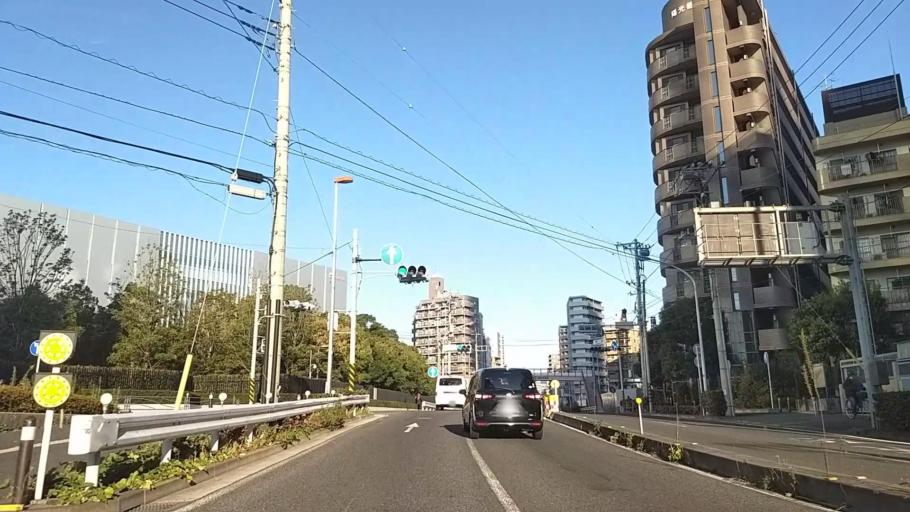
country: JP
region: Kanagawa
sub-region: Kawasaki-shi
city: Kawasaki
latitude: 35.5291
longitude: 139.6922
